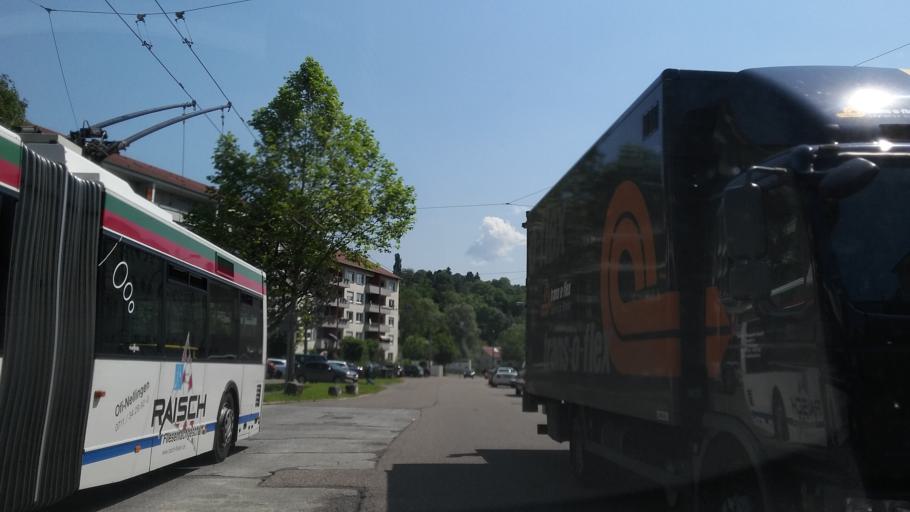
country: DE
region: Baden-Wuerttemberg
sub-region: Regierungsbezirk Stuttgart
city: Esslingen
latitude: 48.7345
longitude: 9.3382
